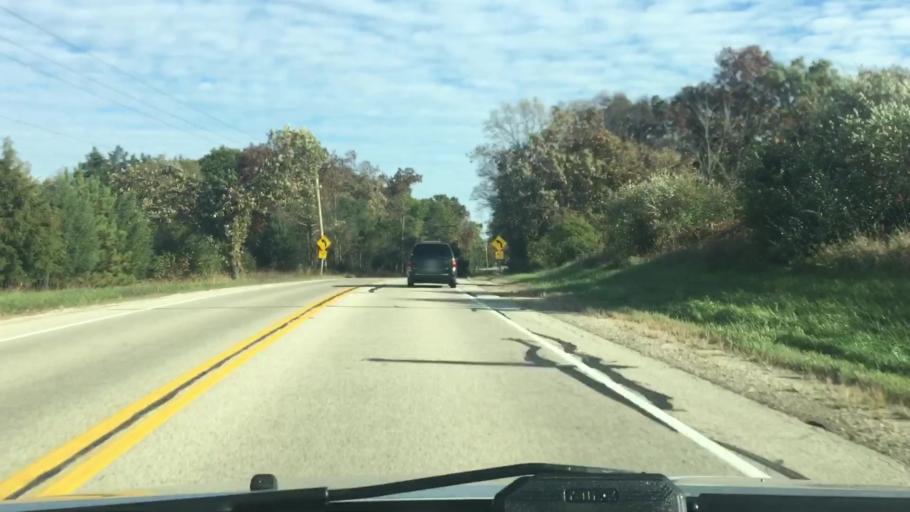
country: US
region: Wisconsin
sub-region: Waukesha County
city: Dousman
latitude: 42.9805
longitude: -88.4658
